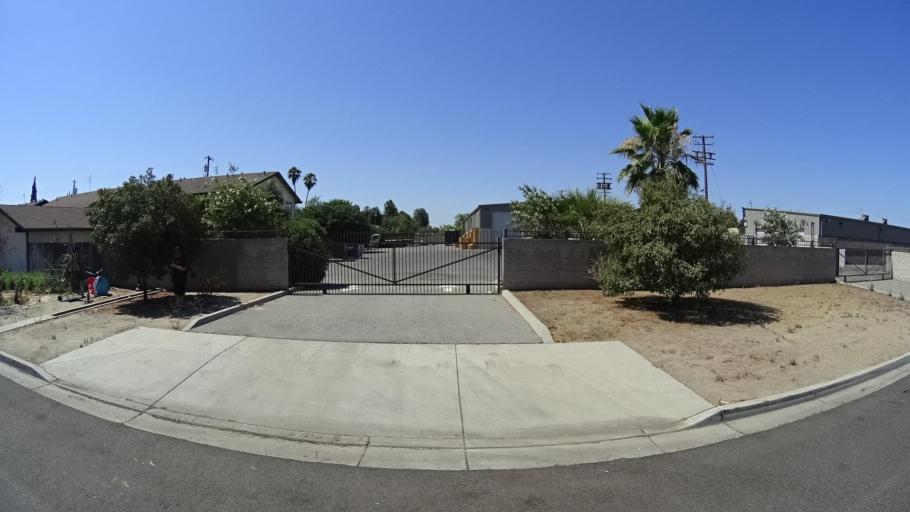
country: US
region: California
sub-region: Fresno County
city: Fresno
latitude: 36.7614
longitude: -119.7400
